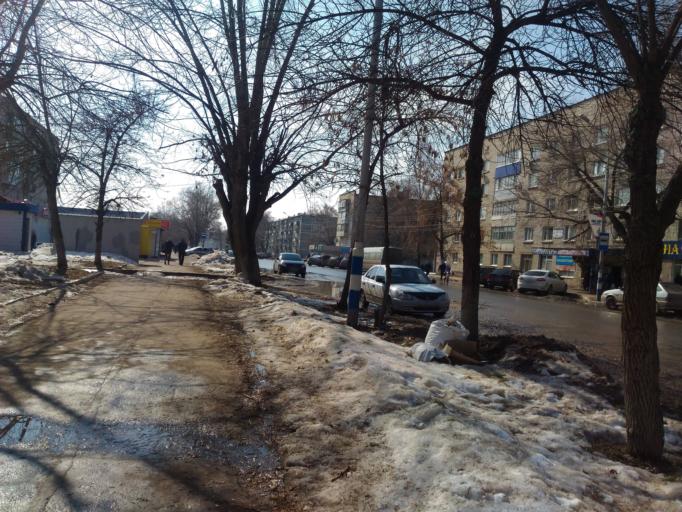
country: RU
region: Ulyanovsk
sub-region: Ulyanovskiy Rayon
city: Ulyanovsk
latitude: 54.3317
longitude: 48.4850
